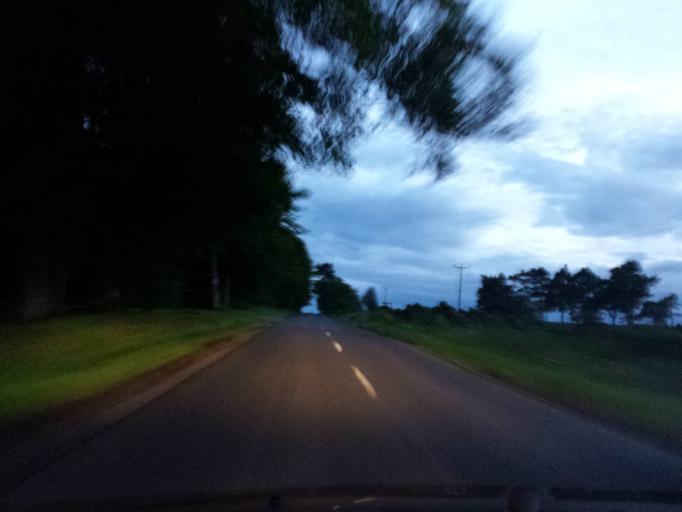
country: GB
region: Scotland
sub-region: The Scottish Borders
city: Duns
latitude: 55.7336
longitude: -2.4360
